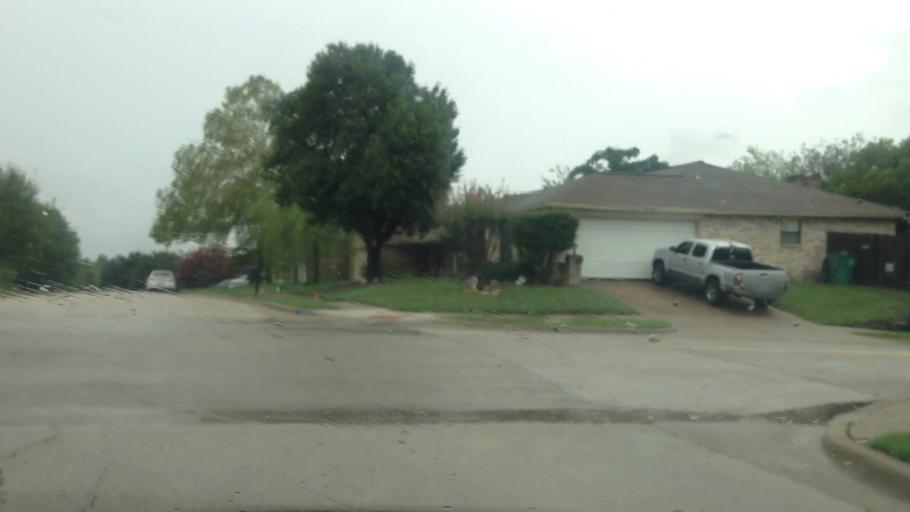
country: US
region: Texas
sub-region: Tarrant County
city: Watauga
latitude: 32.8857
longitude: -97.2444
